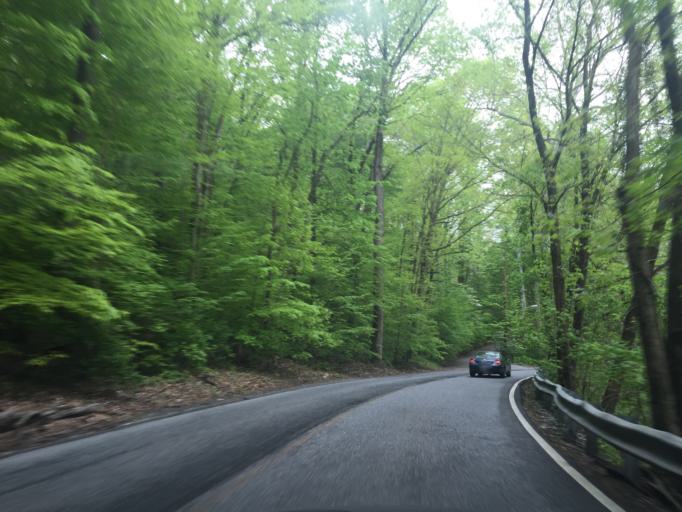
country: US
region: Maryland
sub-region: Baltimore County
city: Charlestown
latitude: 39.3024
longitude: -76.6941
